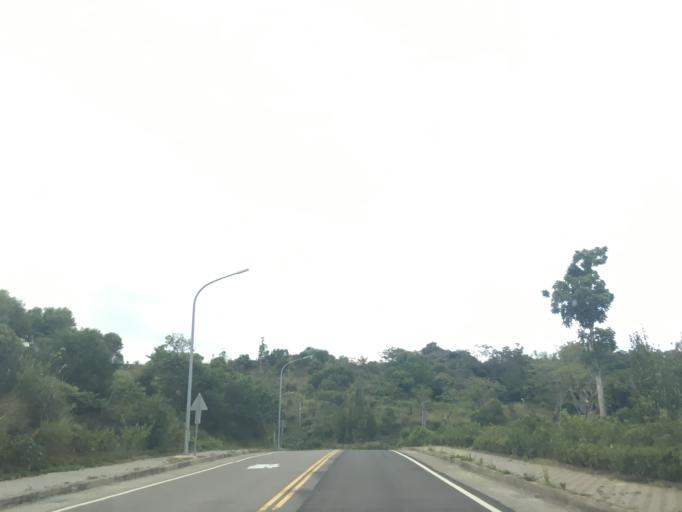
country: TW
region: Taiwan
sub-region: Taichung City
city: Taichung
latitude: 24.1733
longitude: 120.7691
